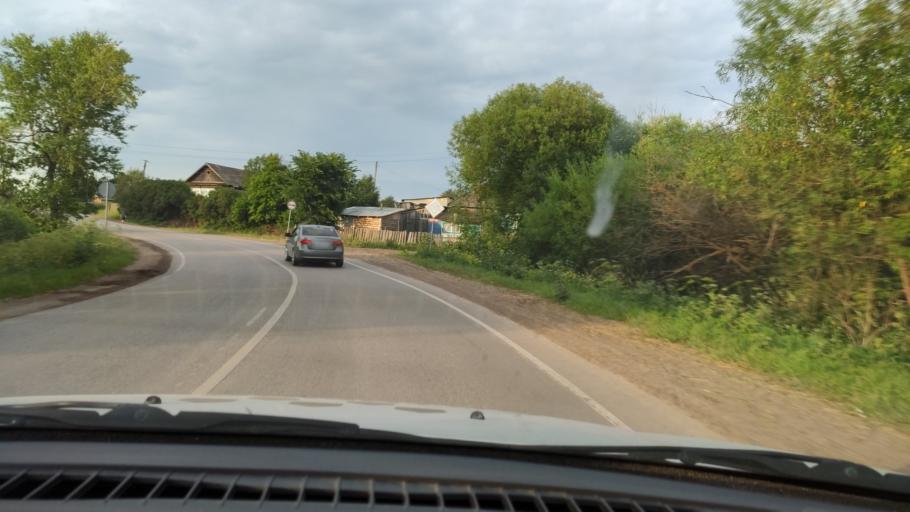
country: RU
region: Perm
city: Kukushtan
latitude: 57.4508
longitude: 56.5216
